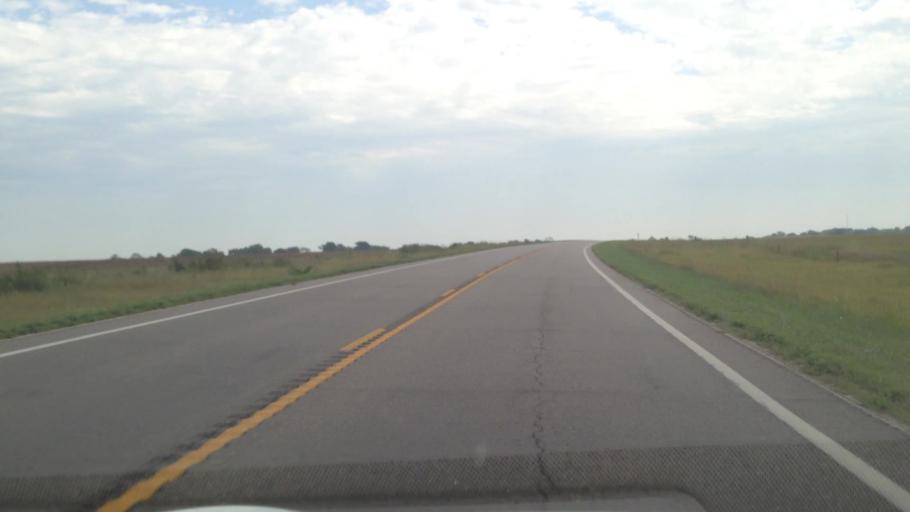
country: US
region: Kansas
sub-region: Bourbon County
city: Fort Scott
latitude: 37.8832
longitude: -95.0145
